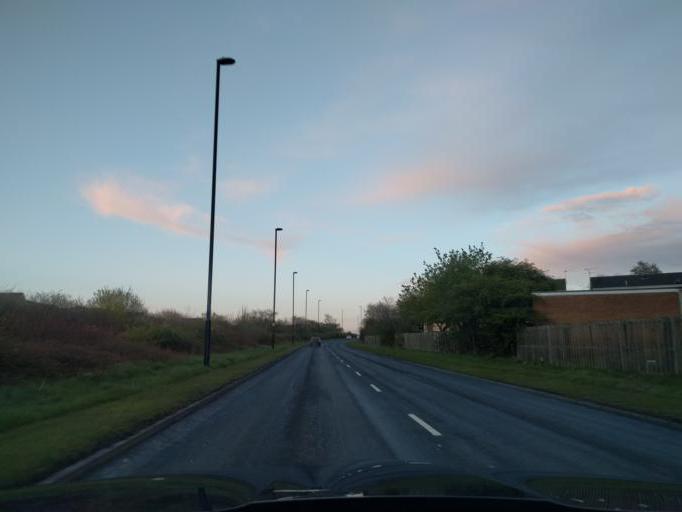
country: GB
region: England
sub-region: Northumberland
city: Seghill
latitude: 55.0409
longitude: -1.5717
